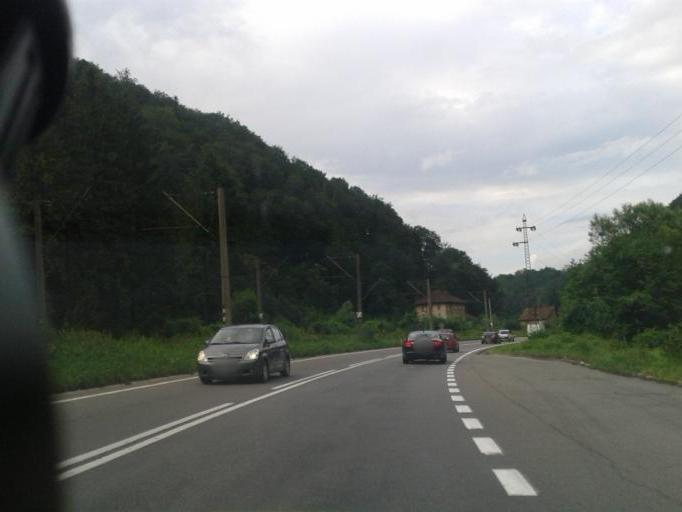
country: RO
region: Brasov
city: Brasov
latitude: 45.5764
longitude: 25.6162
